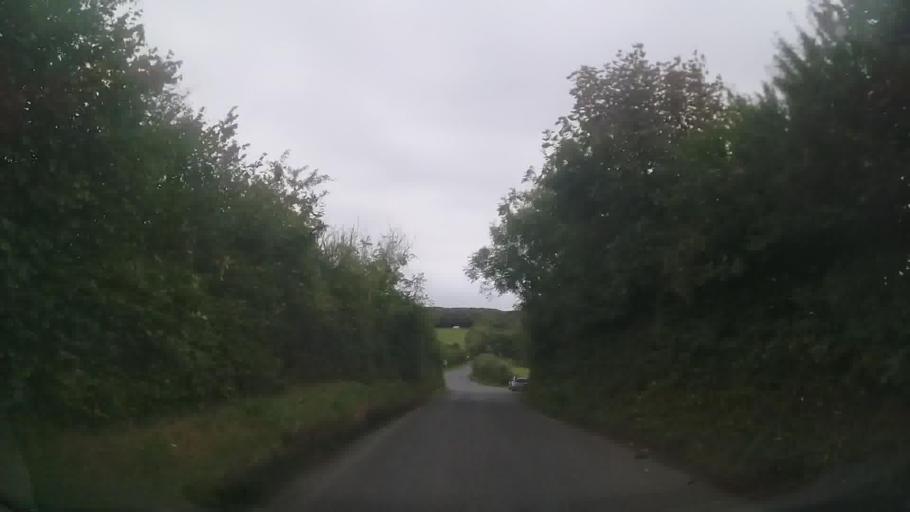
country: GB
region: Wales
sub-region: Pembrokeshire
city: Saundersfoot
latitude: 51.7371
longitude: -4.6366
